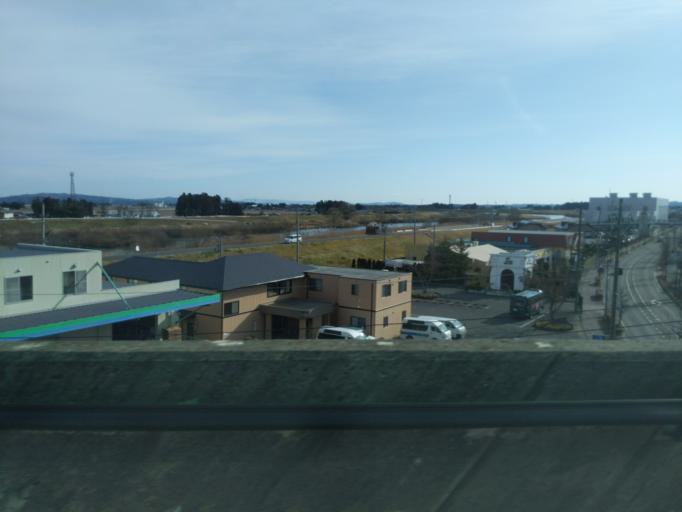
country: JP
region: Miyagi
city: Furukawa
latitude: 38.5862
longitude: 140.9729
